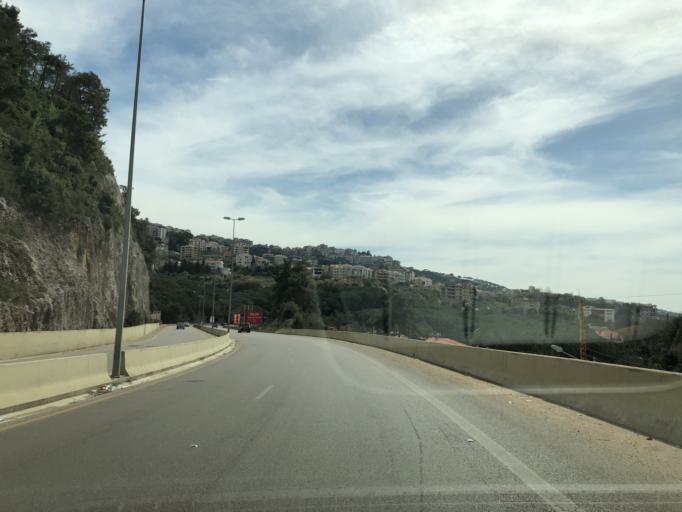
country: LB
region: Mont-Liban
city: Jdaidet el Matn
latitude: 33.8970
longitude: 35.6326
